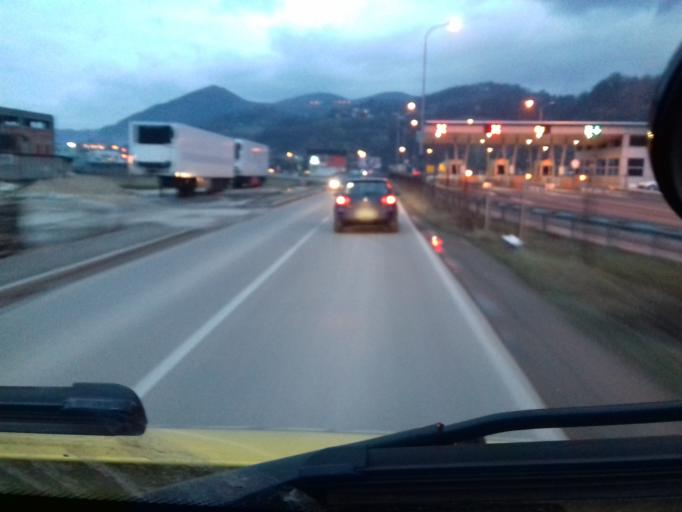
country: BA
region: Federation of Bosnia and Herzegovina
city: Visoko
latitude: 44.0020
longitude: 18.1665
